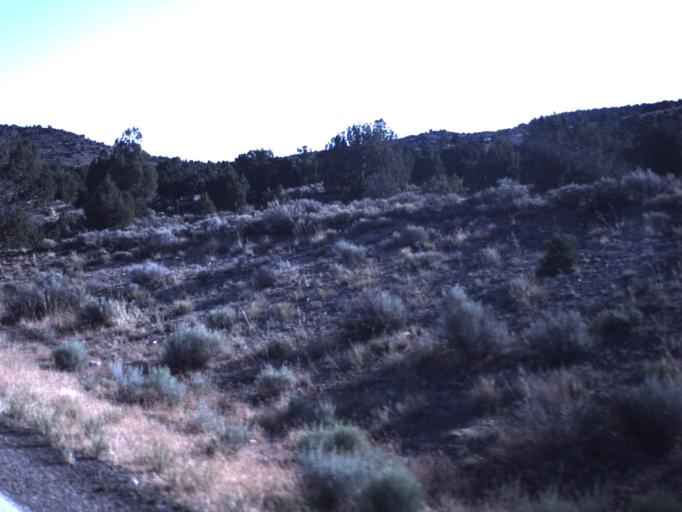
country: US
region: Utah
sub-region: Beaver County
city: Milford
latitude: 38.1216
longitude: -112.9511
